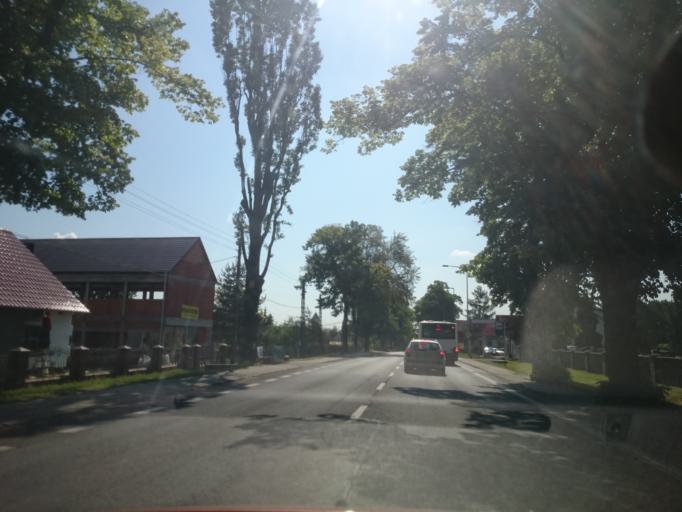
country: PL
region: Opole Voivodeship
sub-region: Powiat opolski
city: Opole
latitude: 50.6475
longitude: 17.9800
